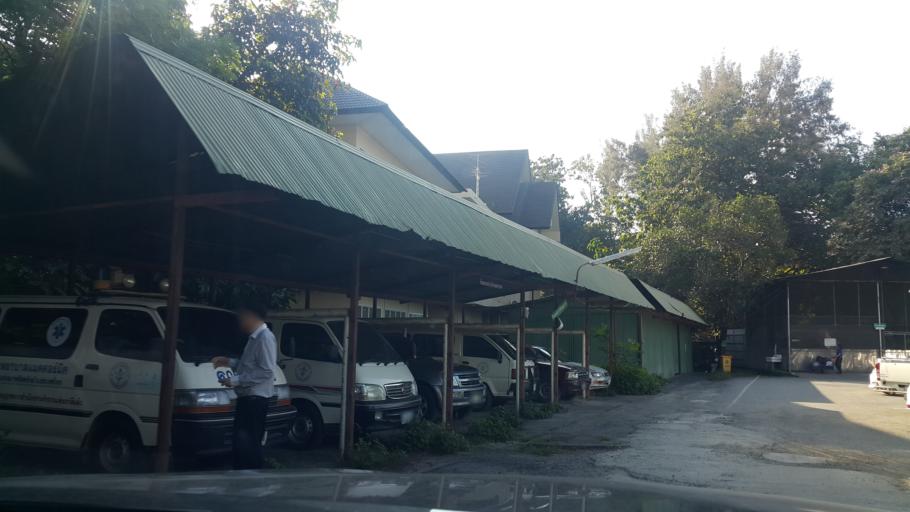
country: TH
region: Chiang Mai
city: Chiang Mai
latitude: 18.7974
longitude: 99.0116
